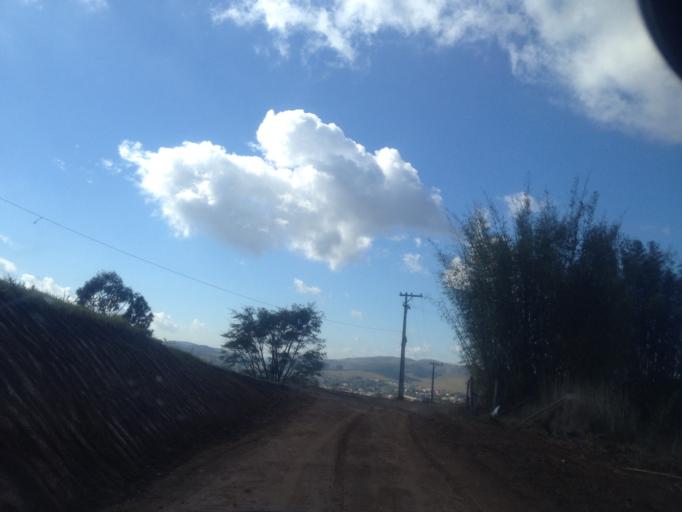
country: BR
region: Rio de Janeiro
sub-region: Porto Real
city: Porto Real
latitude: -22.4367
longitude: -44.3196
